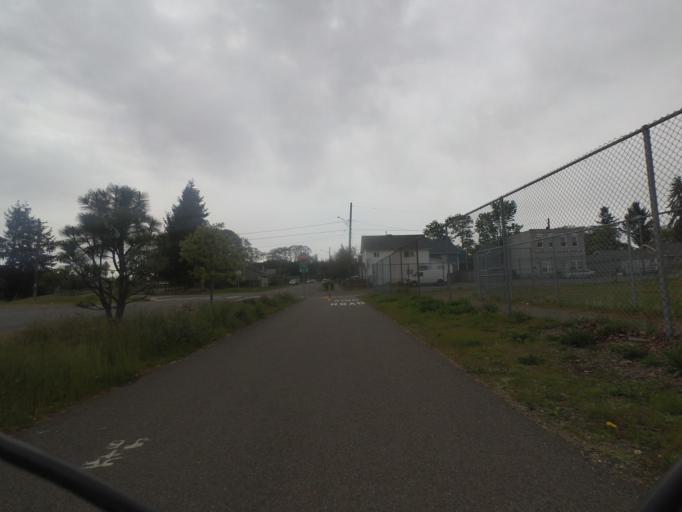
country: US
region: Washington
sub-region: Pierce County
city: Fircrest
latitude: 47.2043
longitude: -122.4768
